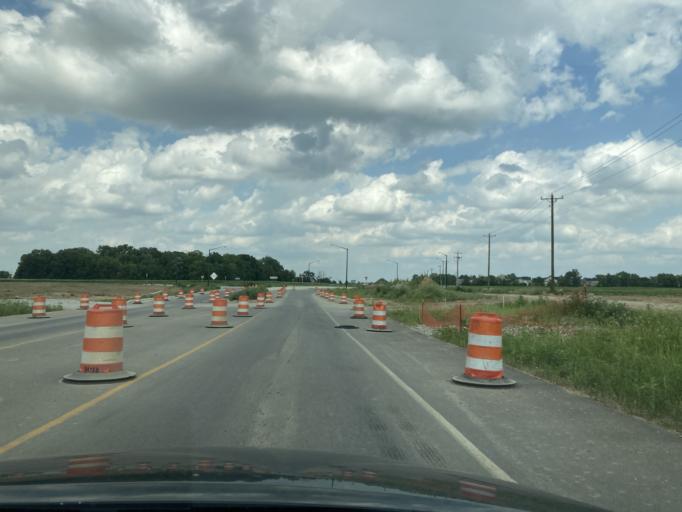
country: US
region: Indiana
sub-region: Boone County
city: Zionsville
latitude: 39.9989
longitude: -86.2236
